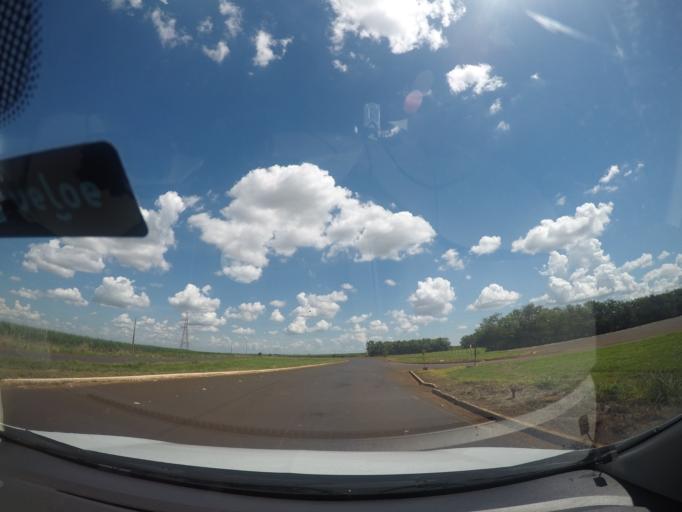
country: BR
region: Minas Gerais
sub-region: Frutal
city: Frutal
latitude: -19.8171
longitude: -48.7311
